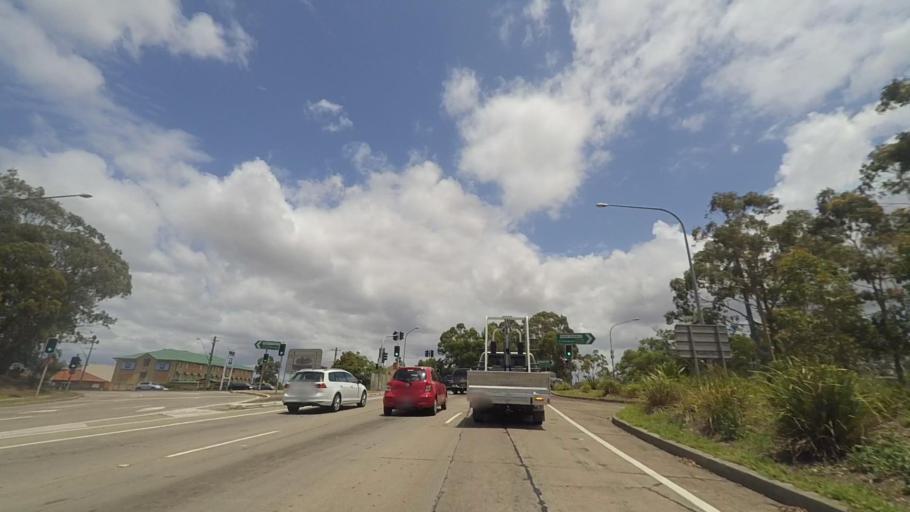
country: AU
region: New South Wales
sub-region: Campbelltown Municipality
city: Glenfield
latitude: -33.9386
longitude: 150.9139
